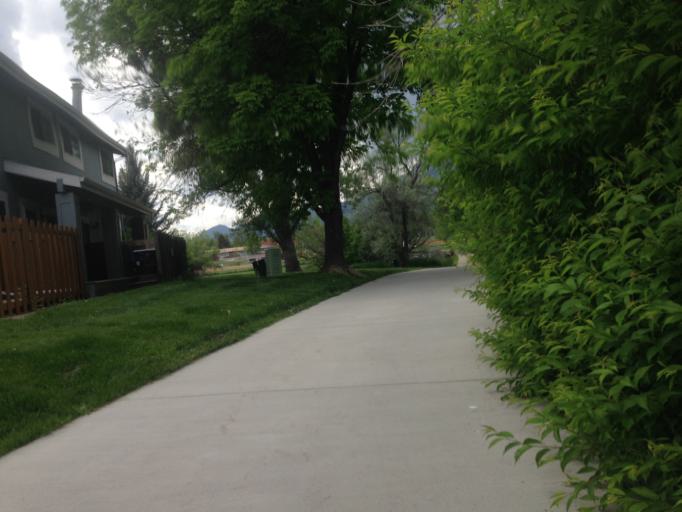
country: US
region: Colorado
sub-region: Boulder County
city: Boulder
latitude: 40.0065
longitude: -105.2432
